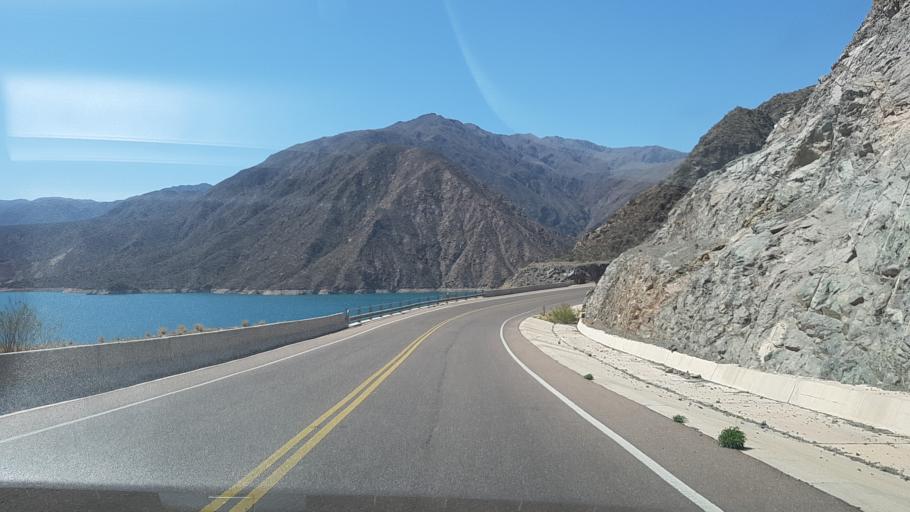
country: AR
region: Mendoza
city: Lujan de Cuyo
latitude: -32.9919
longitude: -69.1560
